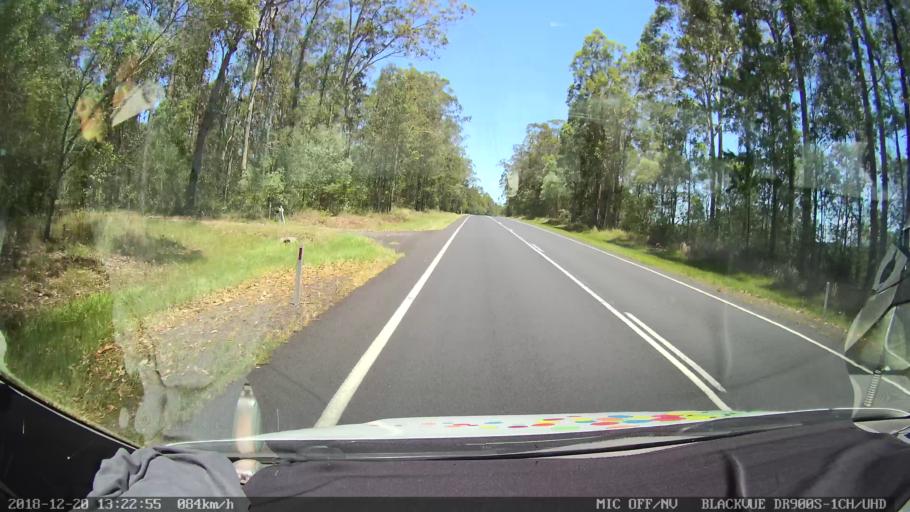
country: AU
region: New South Wales
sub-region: Richmond Valley
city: Casino
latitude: -29.0978
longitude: 153.0010
